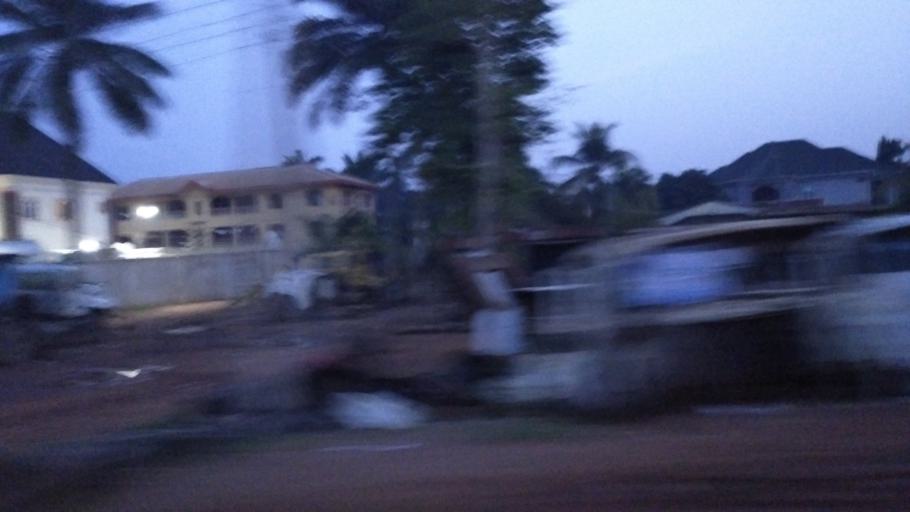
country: NG
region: Enugu
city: Enugu
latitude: 6.4653
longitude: 7.5927
